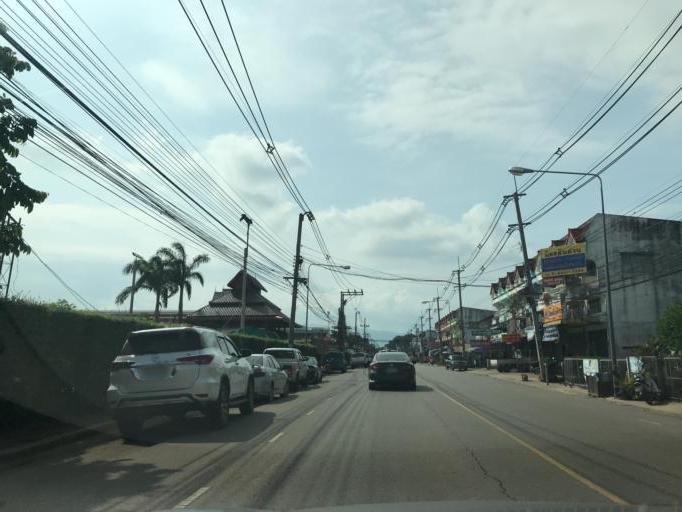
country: TH
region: Phayao
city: Chiang Kham
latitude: 19.5195
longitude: 100.3099
